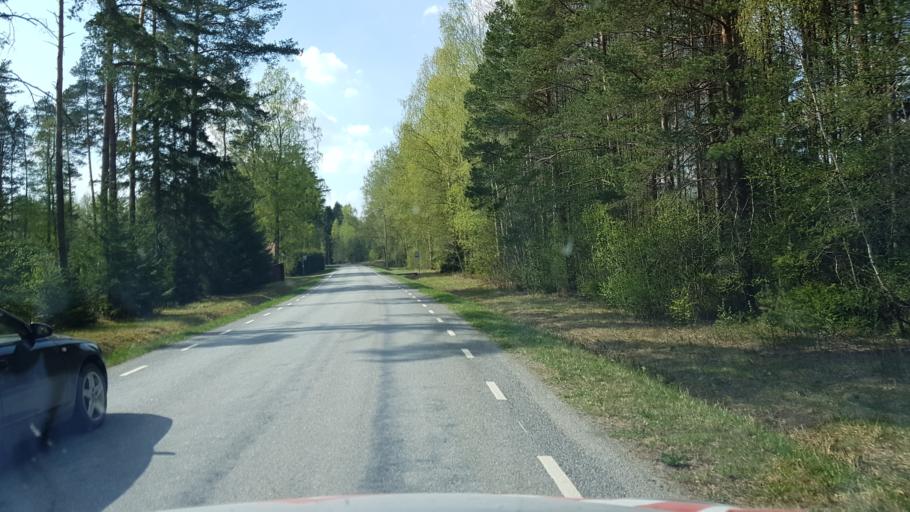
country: EE
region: Paernumaa
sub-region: Paikuse vald
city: Paikuse
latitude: 58.4440
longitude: 24.5928
